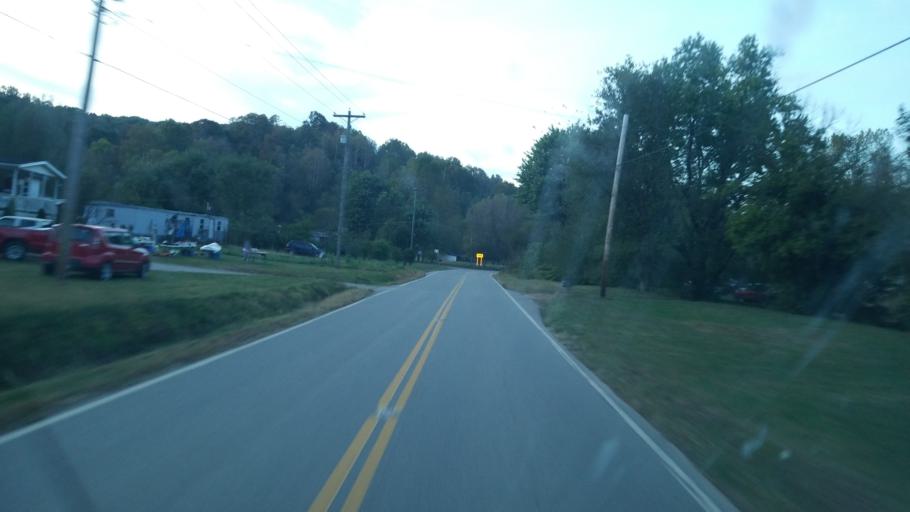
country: US
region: Ohio
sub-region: Meigs County
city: Pomeroy
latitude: 39.0449
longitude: -82.0637
